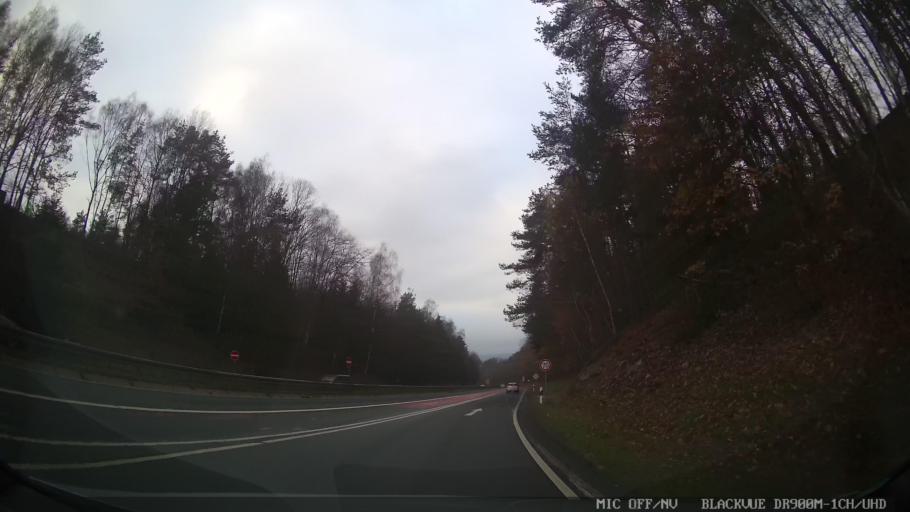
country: DE
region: Hesse
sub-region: Regierungsbezirk Giessen
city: Marburg an der Lahn
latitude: 50.8009
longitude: 8.8010
